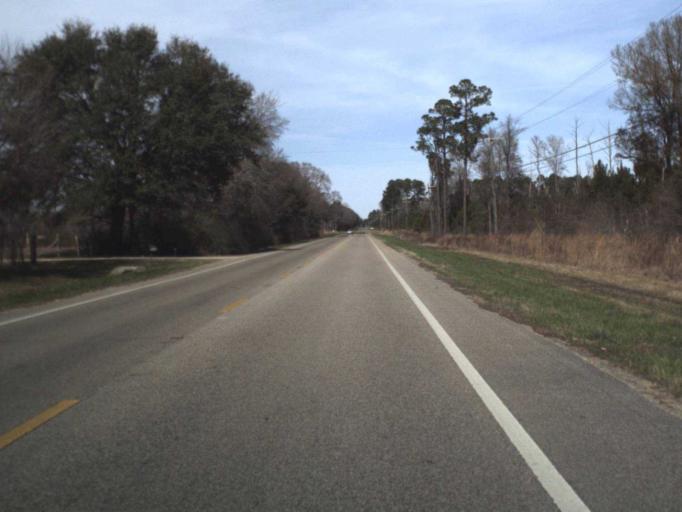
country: US
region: Florida
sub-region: Jackson County
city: Graceville
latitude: 30.9152
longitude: -85.5210
